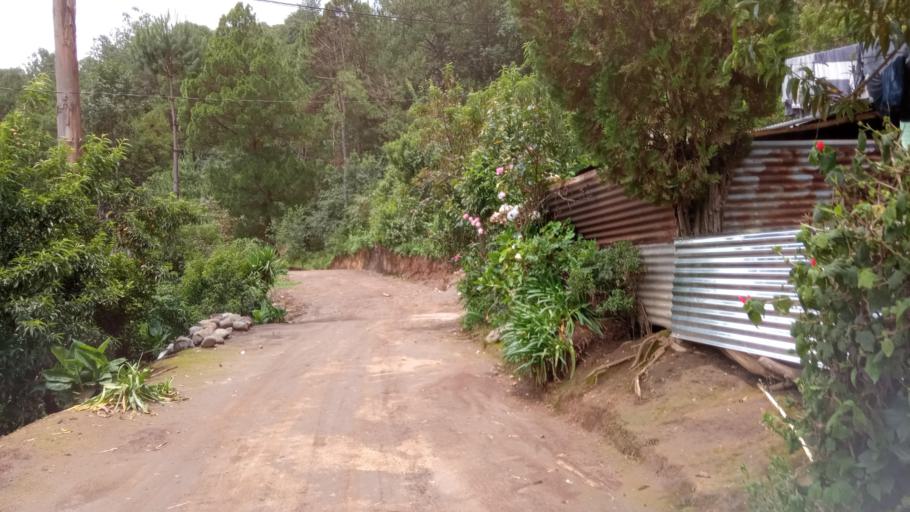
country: GT
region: San Marcos
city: Tejutla
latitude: 15.1159
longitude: -91.8052
